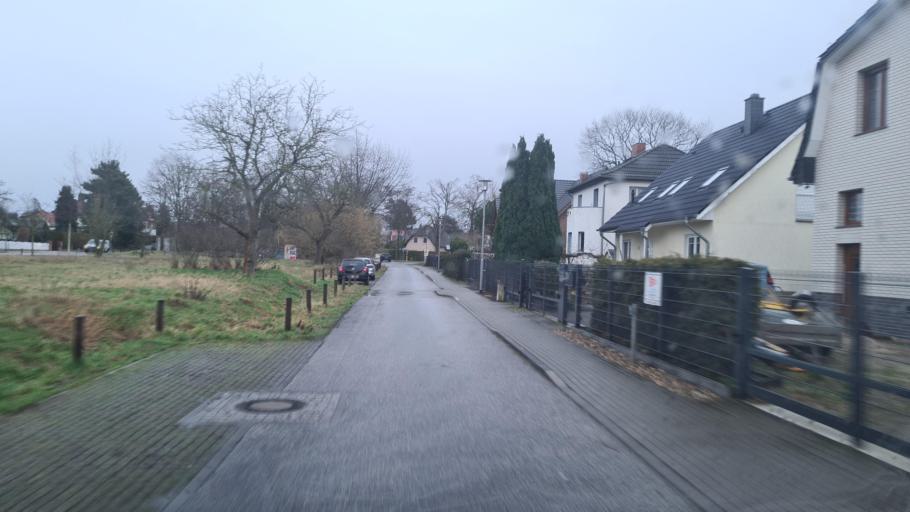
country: DE
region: Brandenburg
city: Teltow
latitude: 52.3889
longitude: 13.2860
